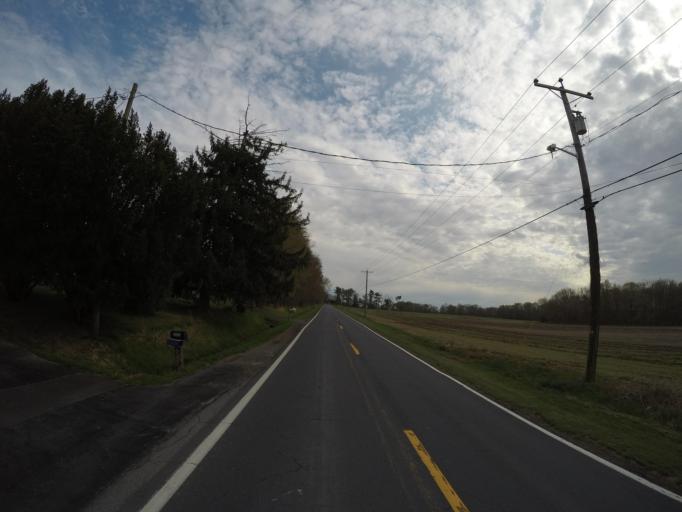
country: US
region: Delaware
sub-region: New Castle County
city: Glasgow
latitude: 39.5677
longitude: -75.7636
